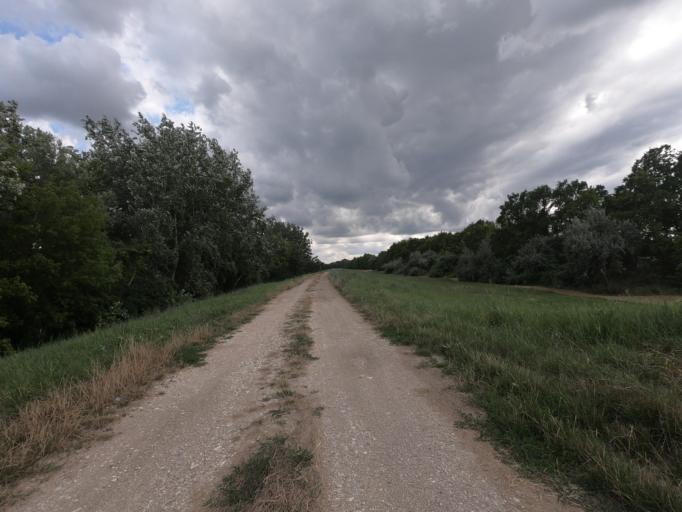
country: HU
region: Heves
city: Poroszlo
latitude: 47.6813
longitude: 20.7121
